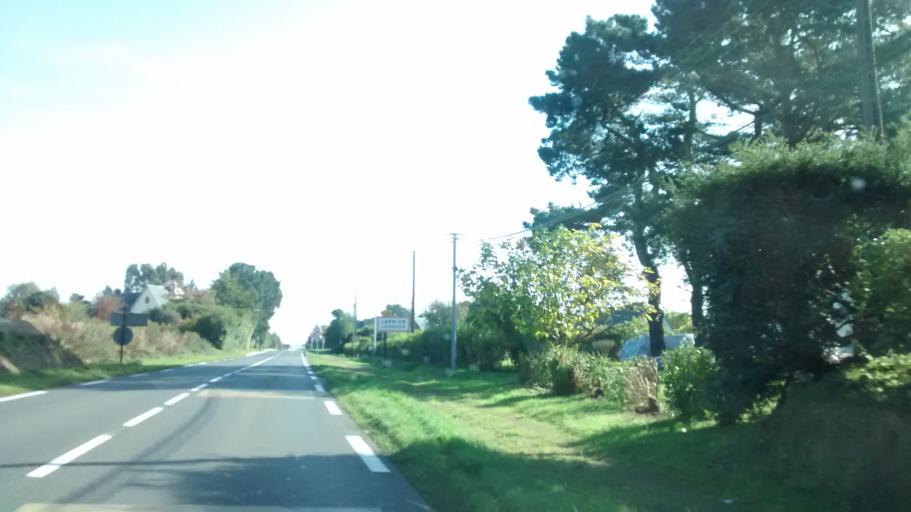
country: FR
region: Brittany
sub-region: Departement des Cotes-d'Armor
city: Pleumeur-Bodou
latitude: 48.7512
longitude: -3.4939
